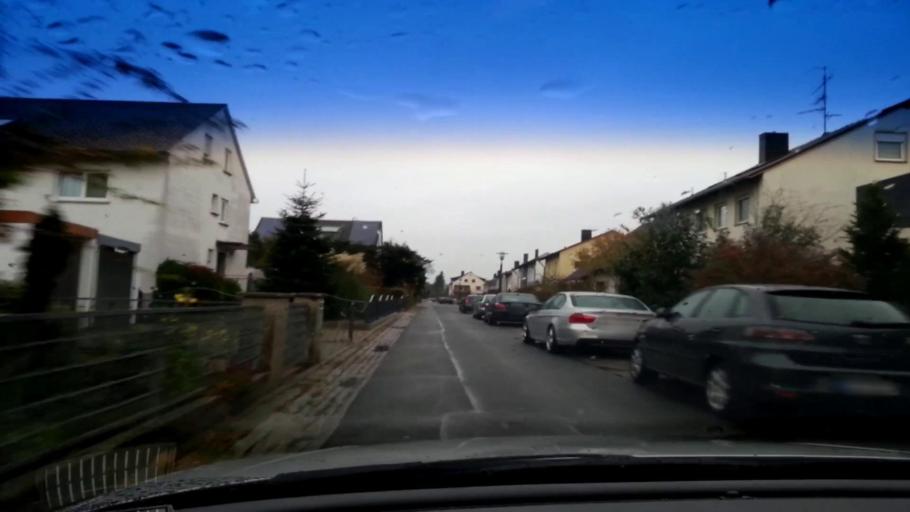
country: DE
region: Bavaria
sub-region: Upper Franconia
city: Hallstadt
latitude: 49.9230
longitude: 10.8843
